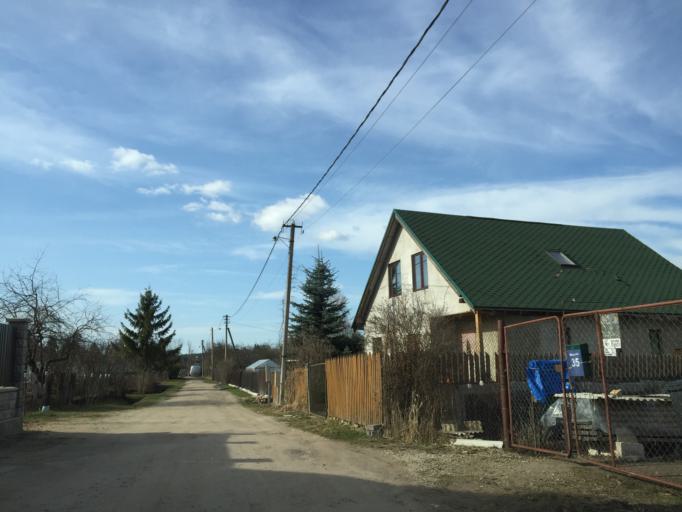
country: LV
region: Ogre
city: Ogre
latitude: 56.8072
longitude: 24.6397
